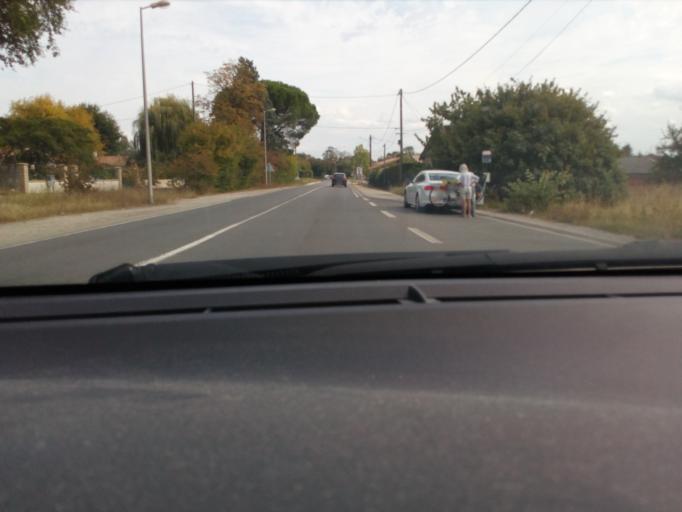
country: FR
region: Poitou-Charentes
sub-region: Departement de la Charente
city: Fleac
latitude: 45.6730
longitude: 0.0976
